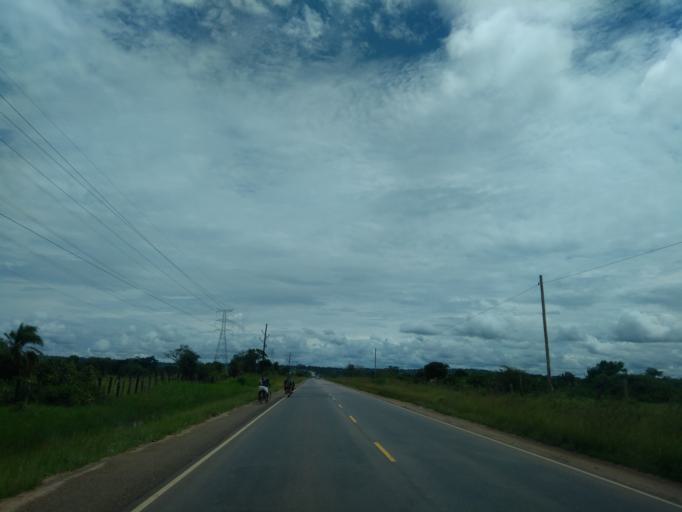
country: UG
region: Central Region
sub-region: Butambala District
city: Gombe
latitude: -0.0276
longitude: 32.0165
